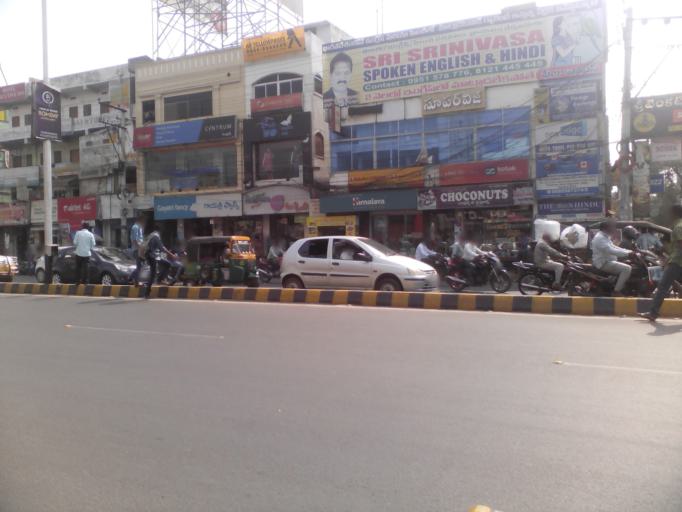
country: IN
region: Andhra Pradesh
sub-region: Krishna
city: Vijayawada
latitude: 16.5031
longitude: 80.6394
